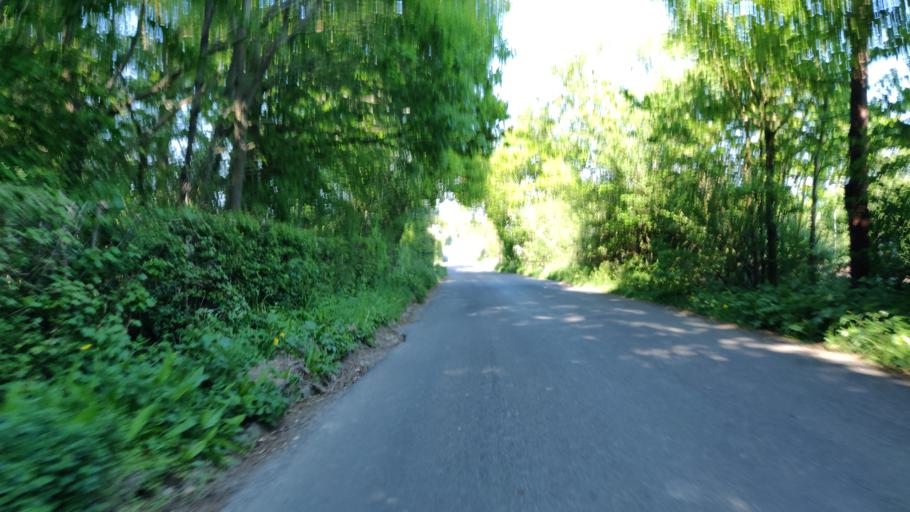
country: GB
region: England
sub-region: West Sussex
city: Southwater
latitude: 51.0258
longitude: -0.4001
